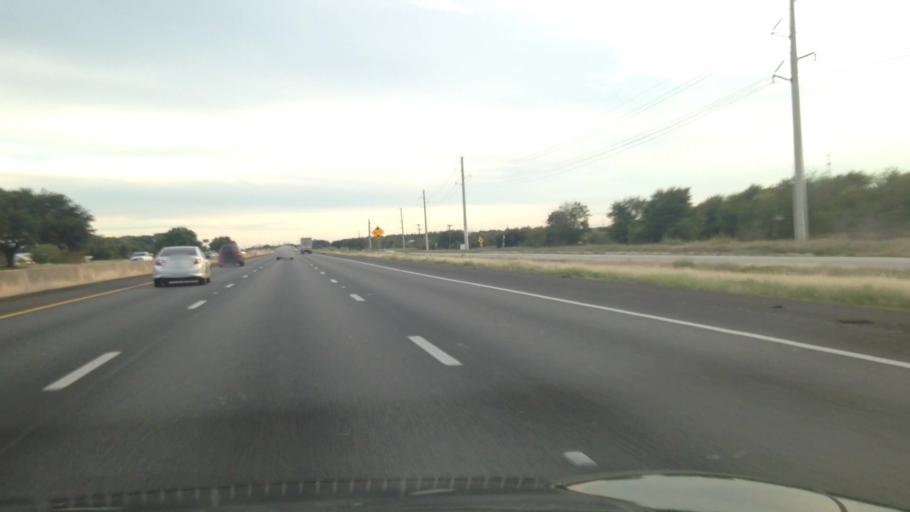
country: US
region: Texas
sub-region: Hays County
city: Kyle
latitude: 29.9630
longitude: -97.8762
